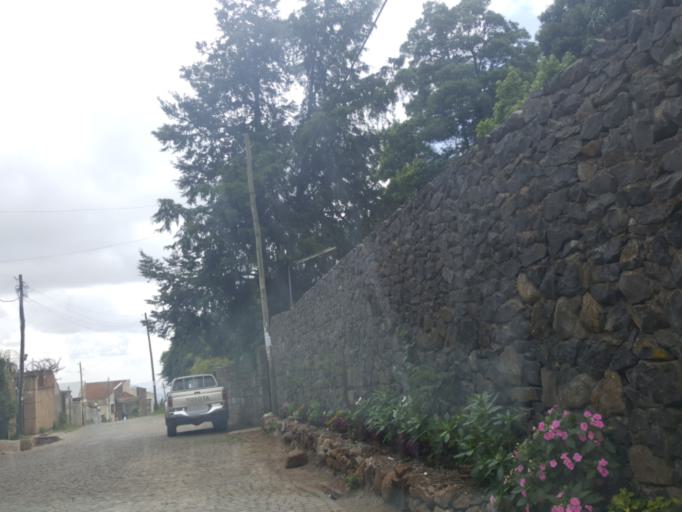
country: ET
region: Adis Abeba
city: Addis Ababa
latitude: 9.0656
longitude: 38.7349
